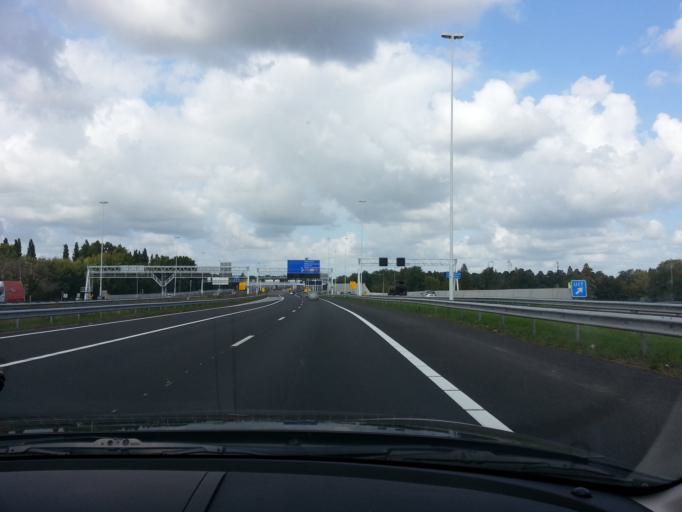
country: NL
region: South Holland
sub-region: Gemeente Schiedam
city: Schiedam
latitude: 51.9094
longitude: 4.3705
